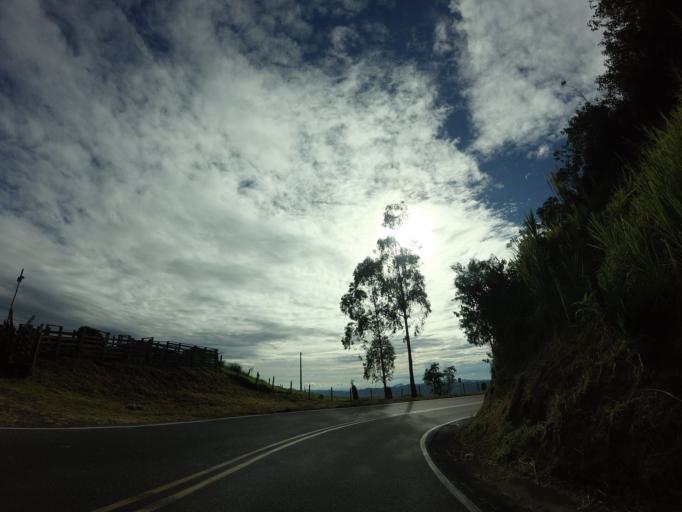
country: CO
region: Tolima
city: Herveo
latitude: 5.1453
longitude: -75.1450
